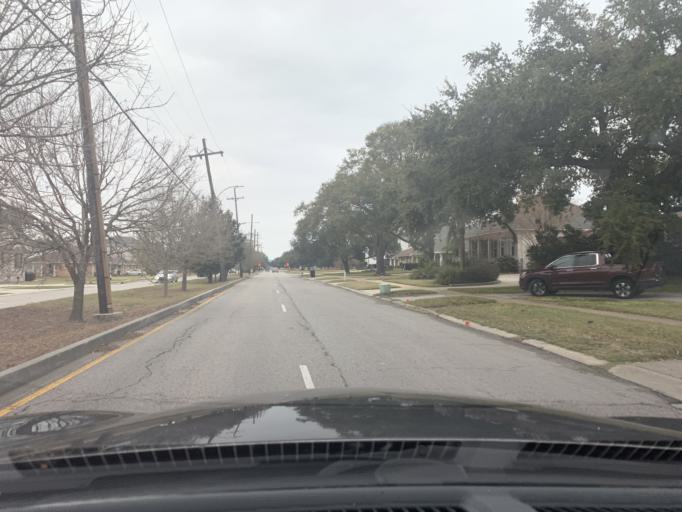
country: US
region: Louisiana
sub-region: Jefferson Parish
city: Metairie
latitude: 30.0193
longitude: -90.1031
